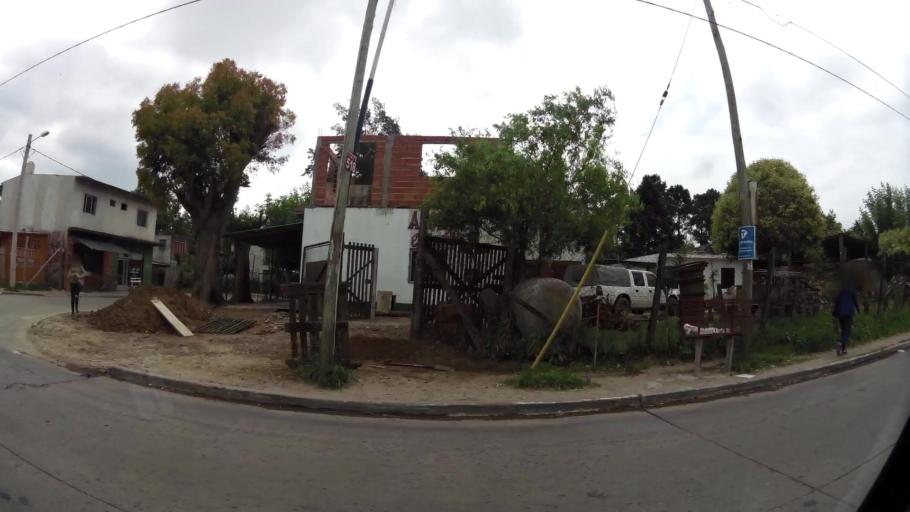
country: AR
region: Buenos Aires
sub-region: Partido de Ezeiza
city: Ezeiza
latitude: -34.8675
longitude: -58.5096
